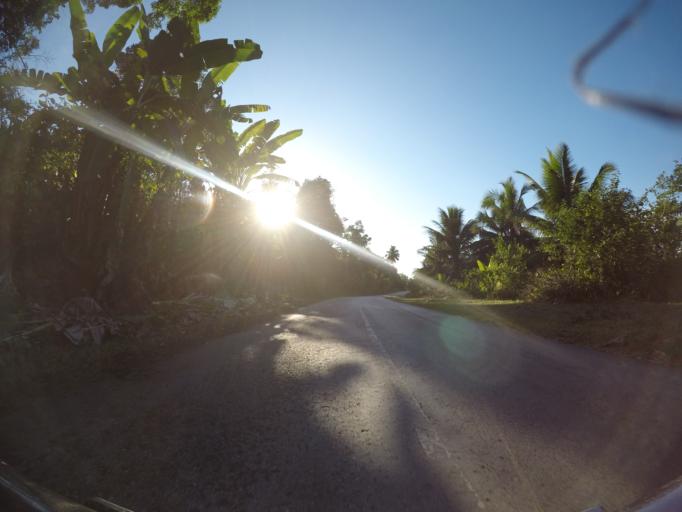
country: TZ
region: Pemba South
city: Mtambile
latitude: -5.3777
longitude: 39.6907
